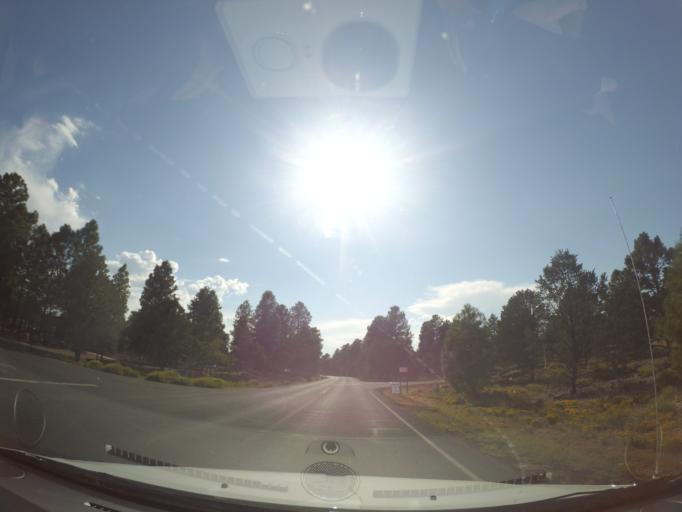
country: US
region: Arizona
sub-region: Coconino County
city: Grand Canyon
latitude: 36.0568
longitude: -112.1150
